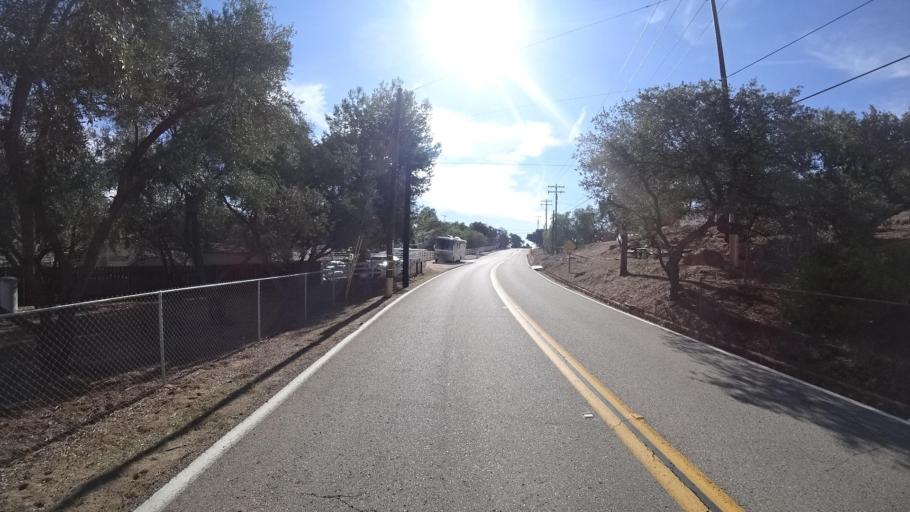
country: US
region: California
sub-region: San Diego County
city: Alpine
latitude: 32.8203
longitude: -116.7851
